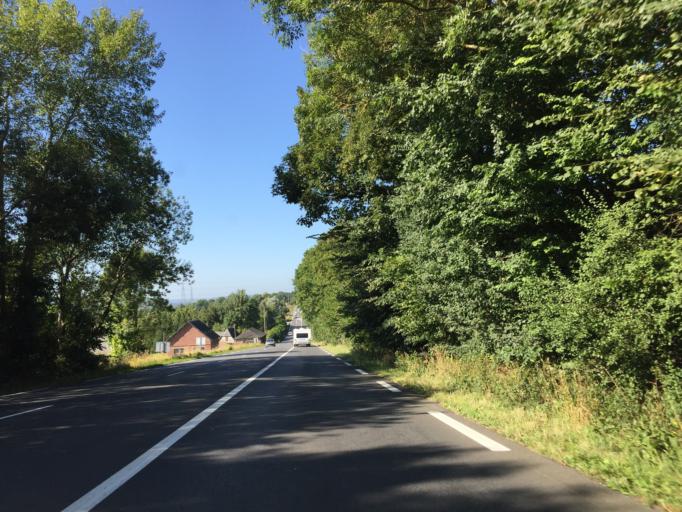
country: FR
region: Lower Normandy
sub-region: Departement du Calvados
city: Lisieux
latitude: 49.2007
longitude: 0.2268
